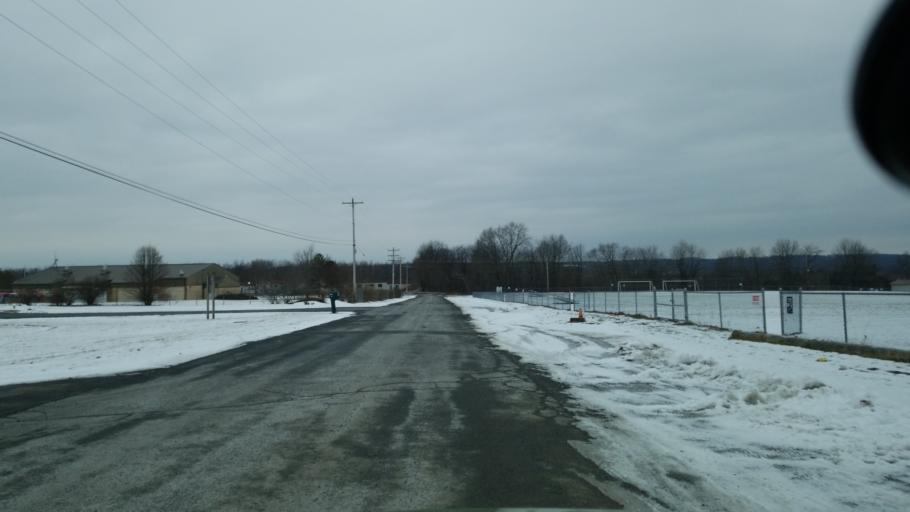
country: US
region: Pennsylvania
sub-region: Clearfield County
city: DuBois
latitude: 41.1086
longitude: -78.7307
